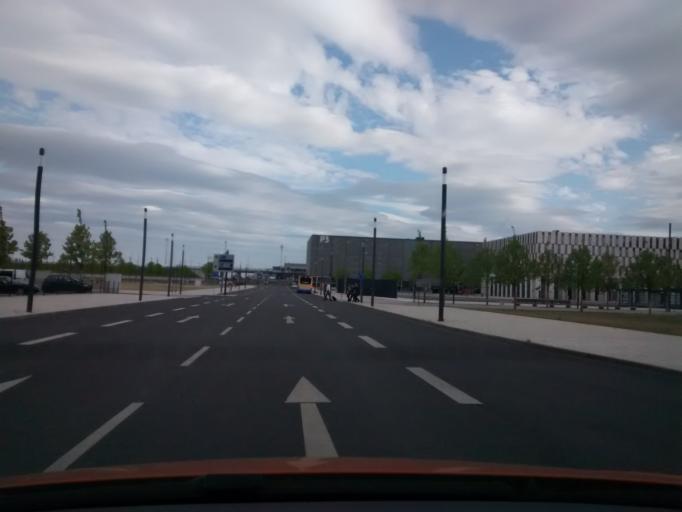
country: DE
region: Brandenburg
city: Schonefeld
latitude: 52.3663
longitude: 13.5121
